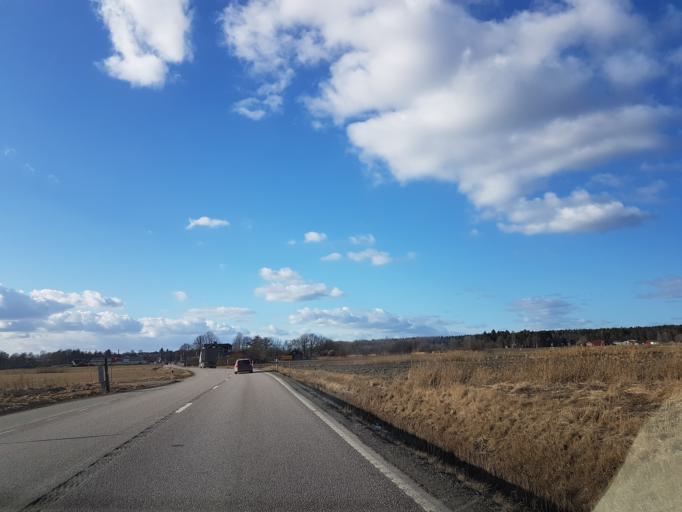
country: SE
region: Stockholm
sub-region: Norrtalje Kommun
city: Rimbo
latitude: 59.7423
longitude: 18.3887
